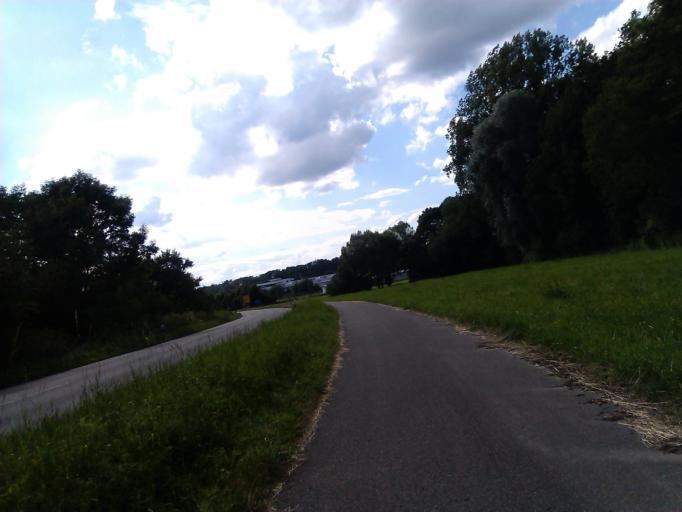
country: DE
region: Baden-Wuerttemberg
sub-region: Karlsruhe Region
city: Ostringen
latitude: 49.2255
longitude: 8.7342
